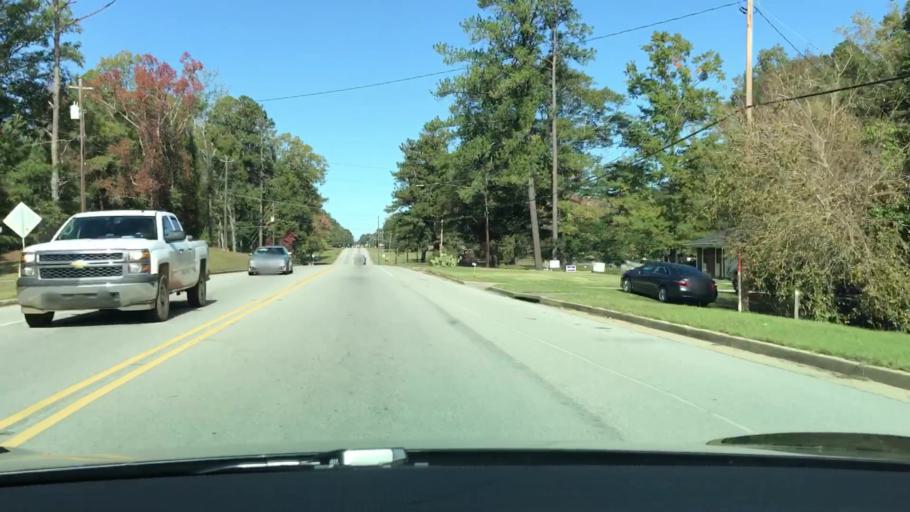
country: US
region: Georgia
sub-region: Warren County
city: West Warrenton
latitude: 33.4090
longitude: -82.6735
